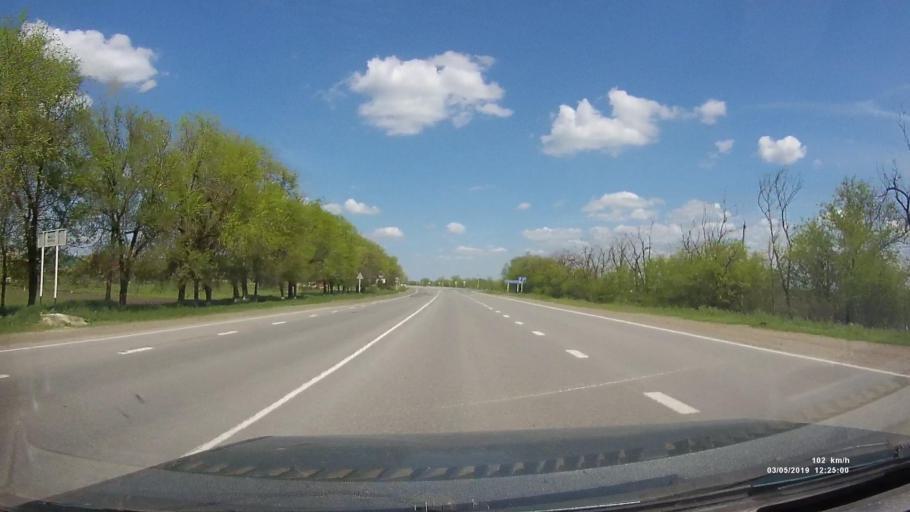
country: RU
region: Rostov
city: Semikarakorsk
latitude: 47.4264
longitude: 40.7072
